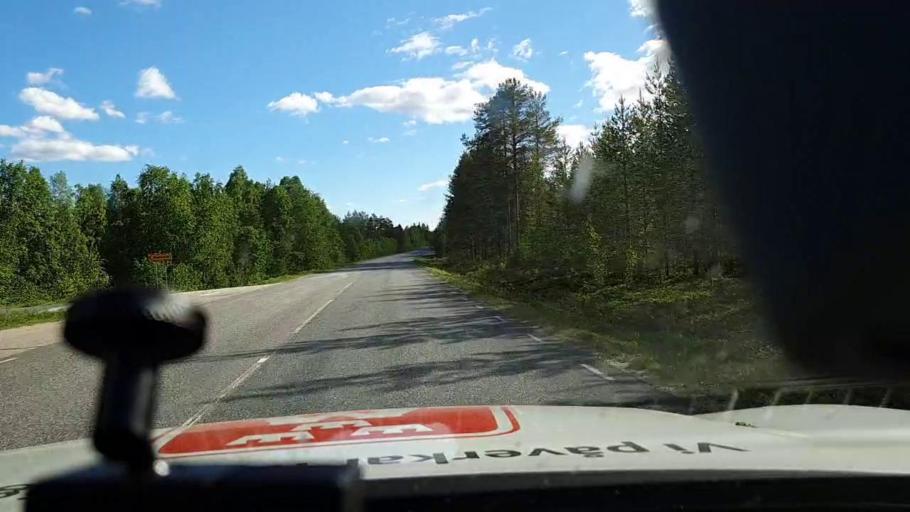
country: FI
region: Lapland
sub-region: Torniolaakso
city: Ylitornio
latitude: 66.3430
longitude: 23.6478
